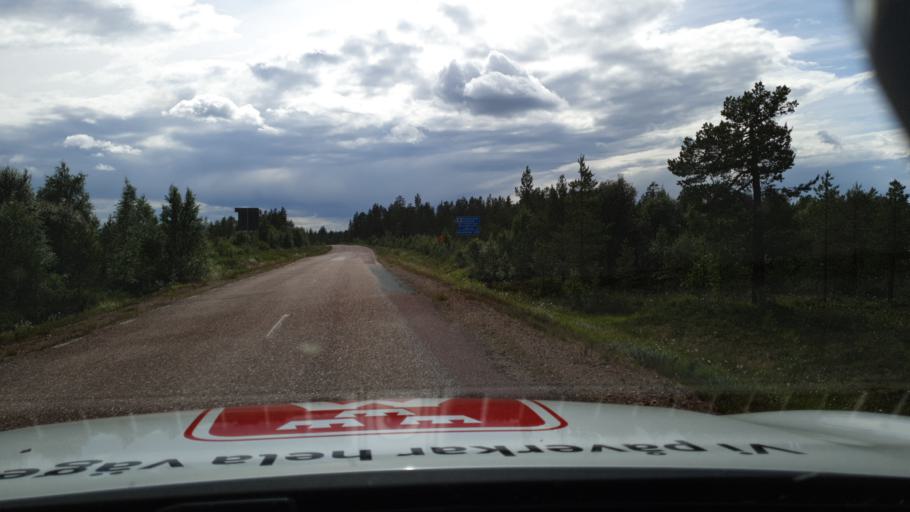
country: SE
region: Dalarna
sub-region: Alvdalens Kommun
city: AElvdalen
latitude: 61.7606
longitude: 13.4609
